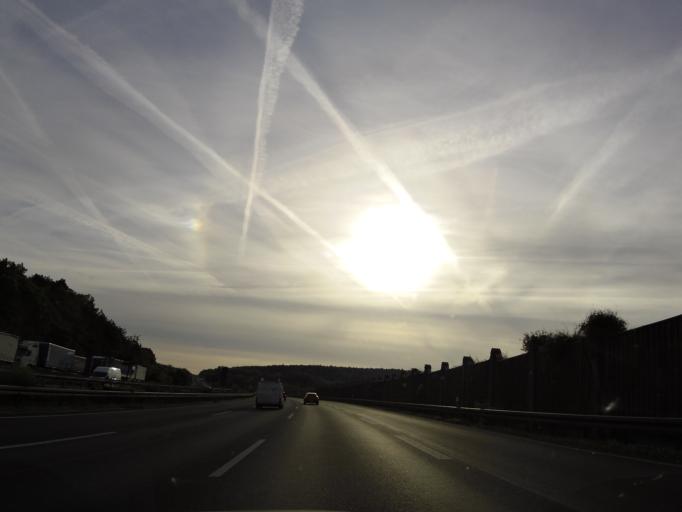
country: DE
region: Lower Saxony
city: Scheden
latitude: 51.3950
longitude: 9.7795
